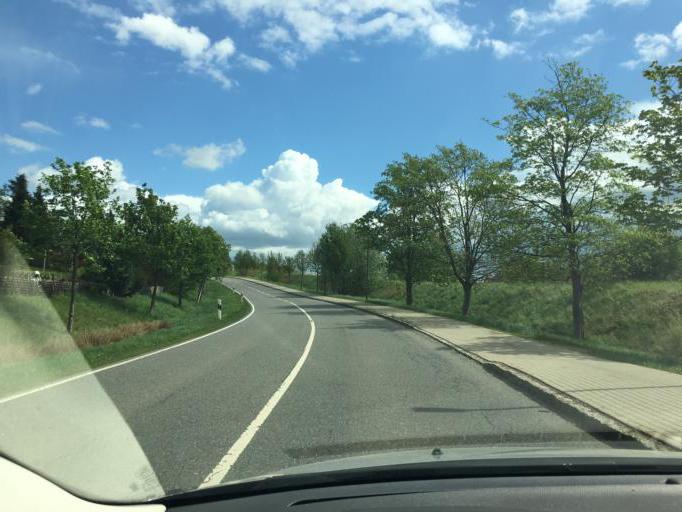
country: DE
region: Saxony
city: Hohenstein-Ernstthal
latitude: 50.8056
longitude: 12.7442
